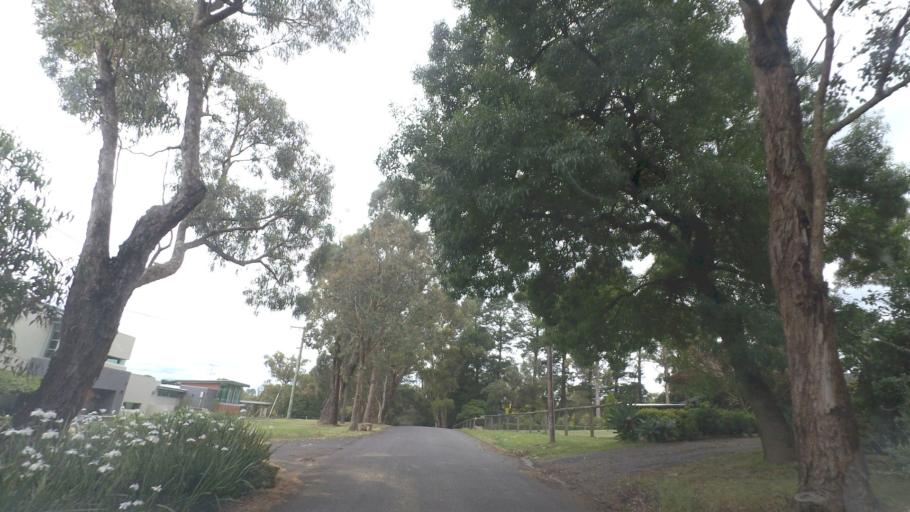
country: AU
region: Victoria
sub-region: Manningham
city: Park Orchards
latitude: -37.7800
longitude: 145.2284
